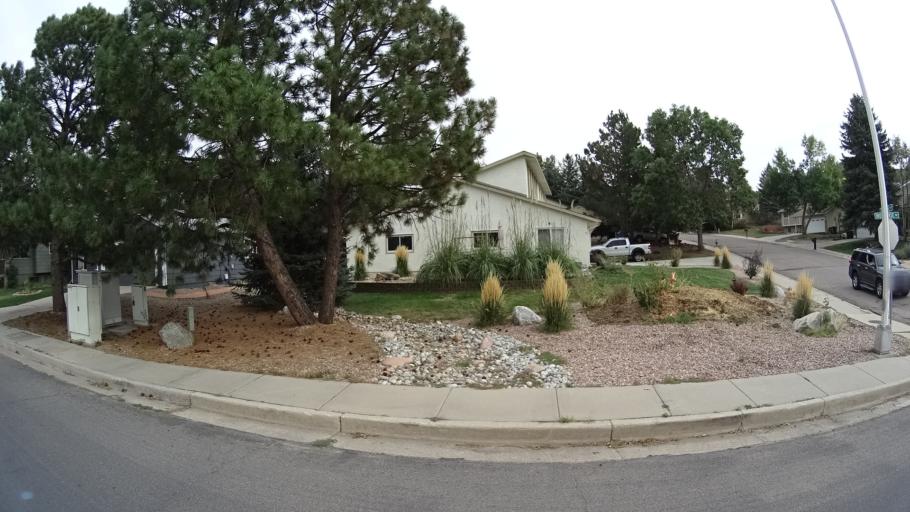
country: US
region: Colorado
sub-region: El Paso County
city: Cimarron Hills
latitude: 38.9014
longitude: -104.7295
